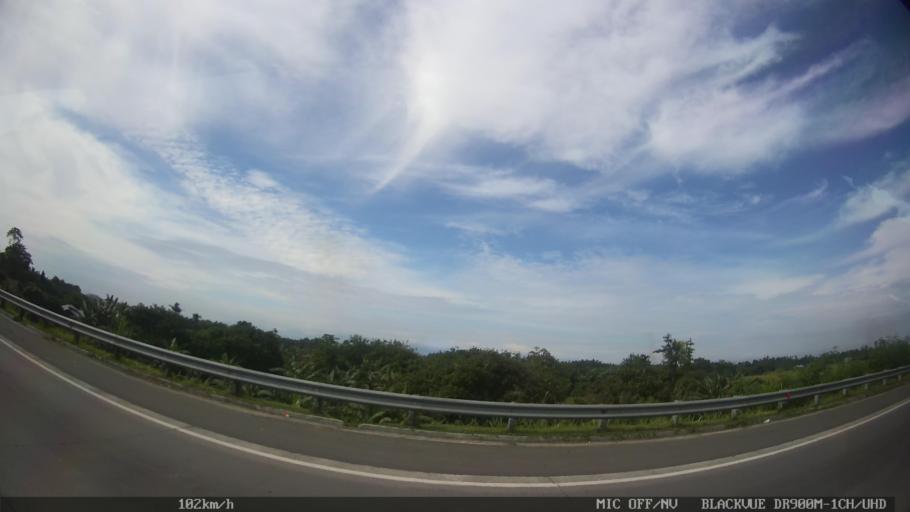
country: ID
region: North Sumatra
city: Sunggal
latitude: 3.6395
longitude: 98.5729
